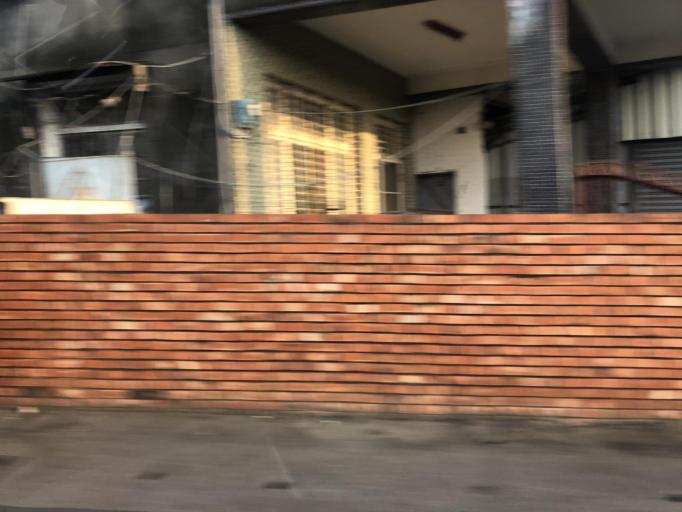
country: TW
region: Taiwan
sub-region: Tainan
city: Tainan
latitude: 23.1345
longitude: 120.2600
